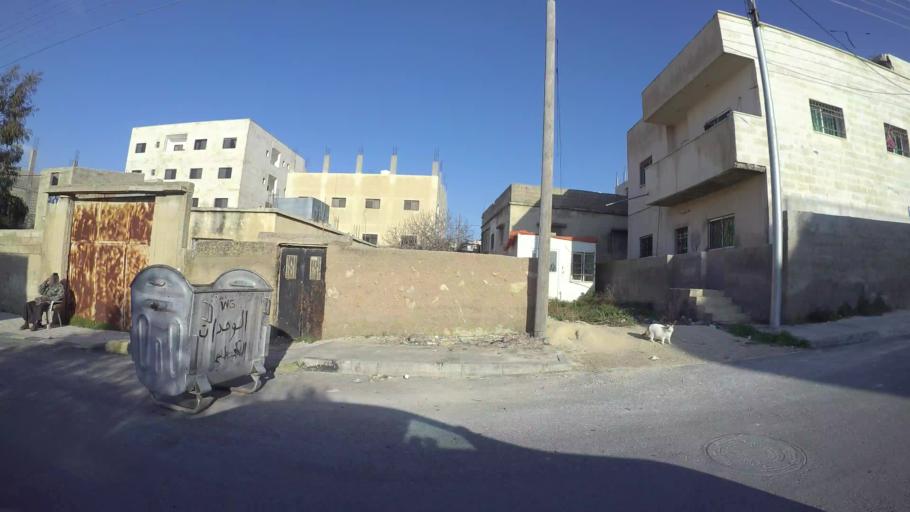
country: JO
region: Amman
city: Al Bunayyat ash Shamaliyah
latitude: 31.9000
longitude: 35.9099
